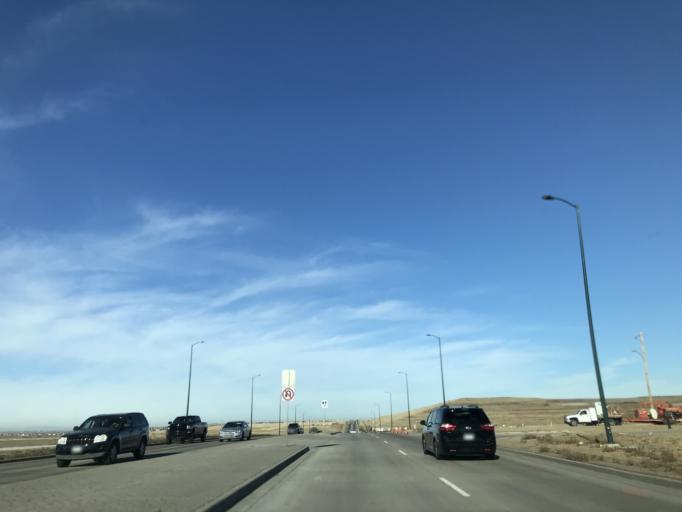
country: US
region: Colorado
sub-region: Adams County
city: Aurora
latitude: 39.8380
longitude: -104.7719
